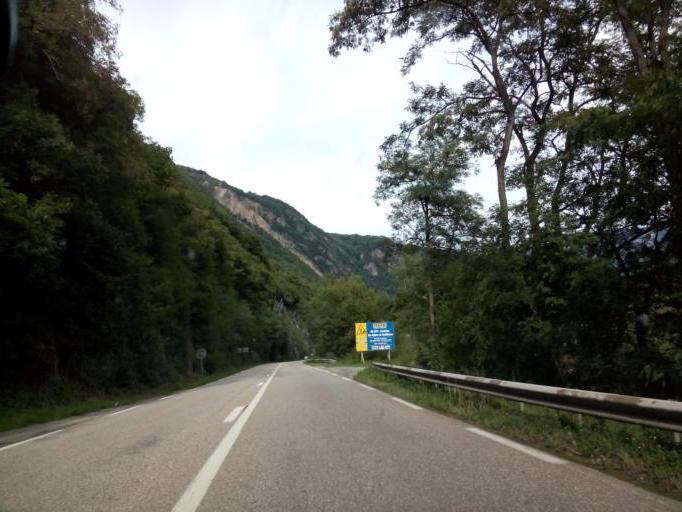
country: FR
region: Rhone-Alpes
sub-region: Departement de l'Isere
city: Vizille
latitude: 45.0523
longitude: 5.7941
